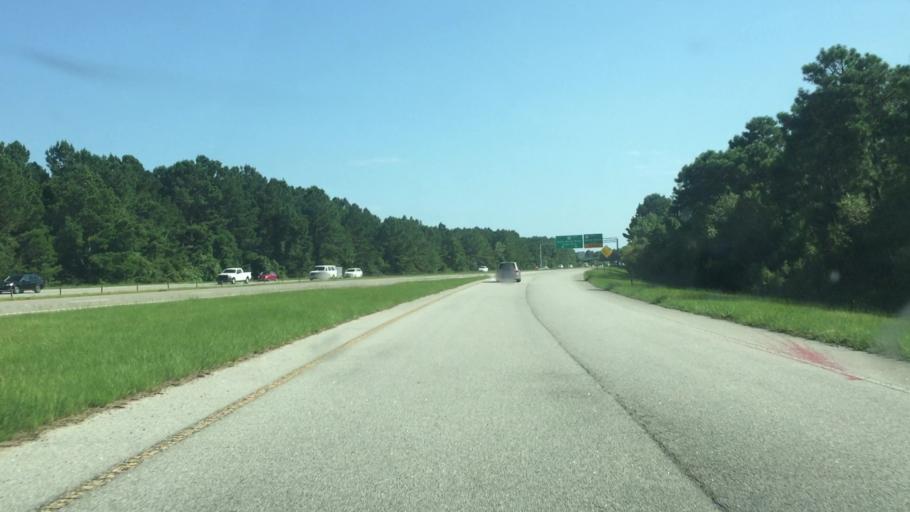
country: US
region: South Carolina
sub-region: Horry County
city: North Myrtle Beach
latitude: 33.8049
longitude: -78.7793
